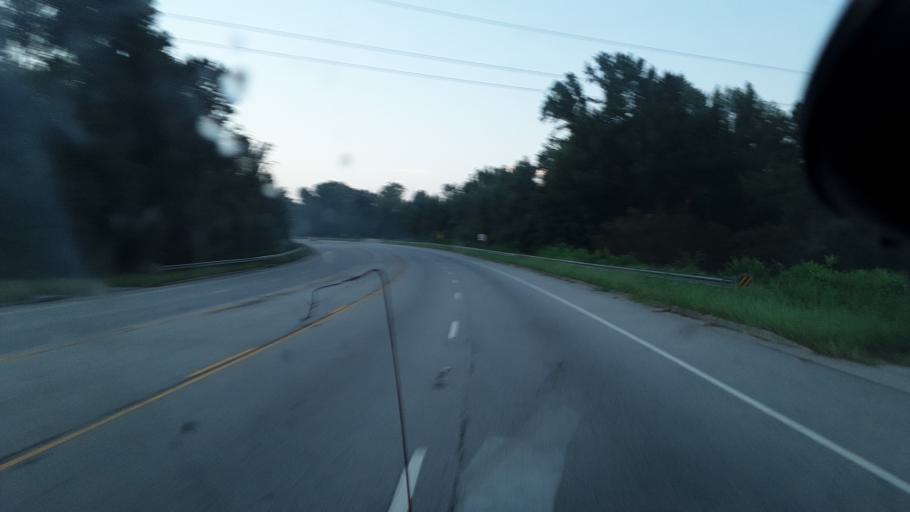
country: US
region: South Carolina
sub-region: Sumter County
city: South Sumter
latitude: 33.8766
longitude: -80.3357
